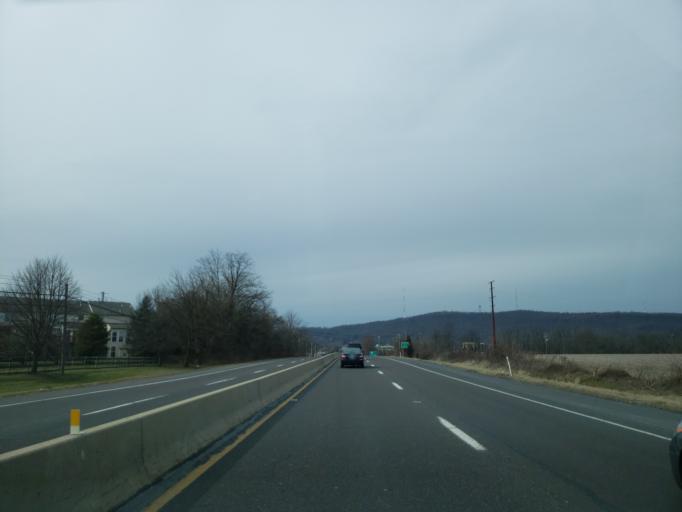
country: US
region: Pennsylvania
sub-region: Lehigh County
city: Coopersburg
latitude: 40.5445
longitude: -75.4192
